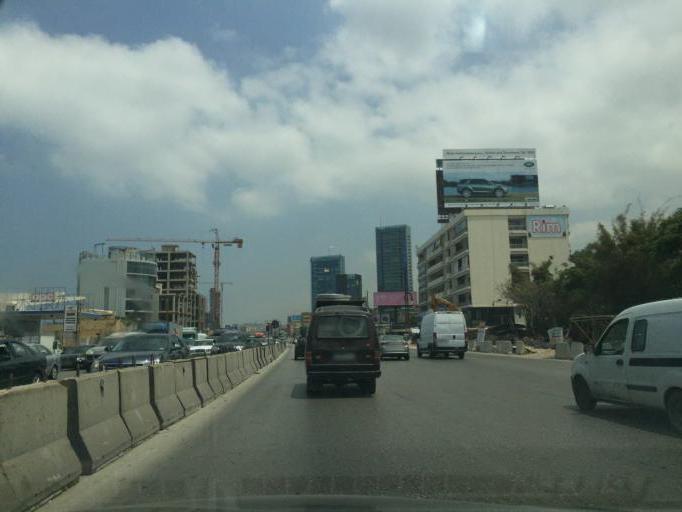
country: LB
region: Mont-Liban
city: Jdaidet el Matn
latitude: 33.9129
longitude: 35.5815
